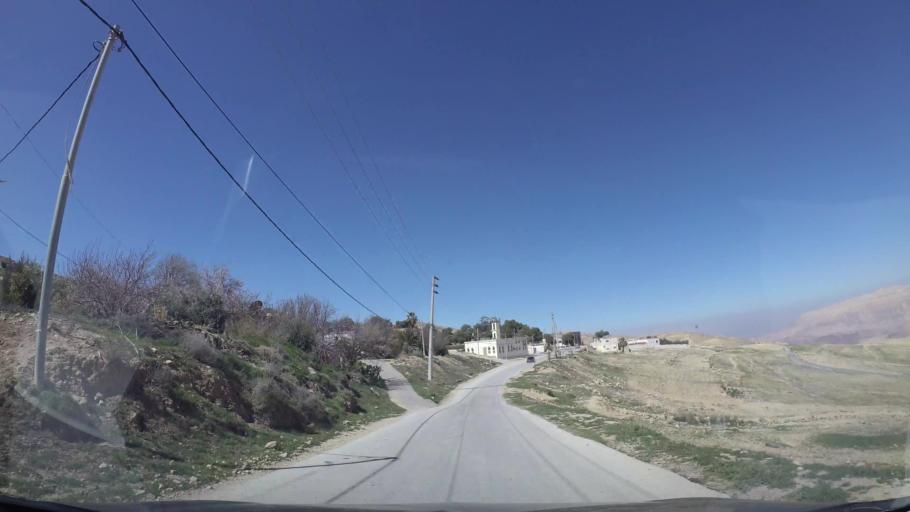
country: JO
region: Tafielah
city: At Tafilah
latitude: 30.8400
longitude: 35.5698
